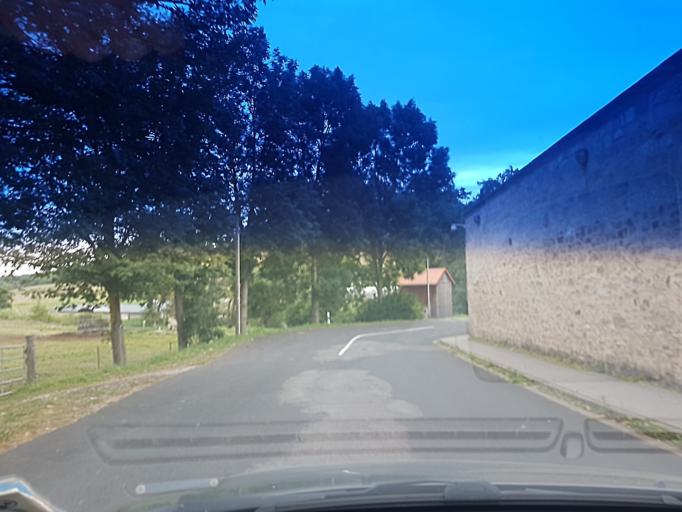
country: DE
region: Bavaria
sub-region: Regierungsbezirk Unterfranken
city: Geiselwind
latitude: 49.8472
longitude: 10.4971
